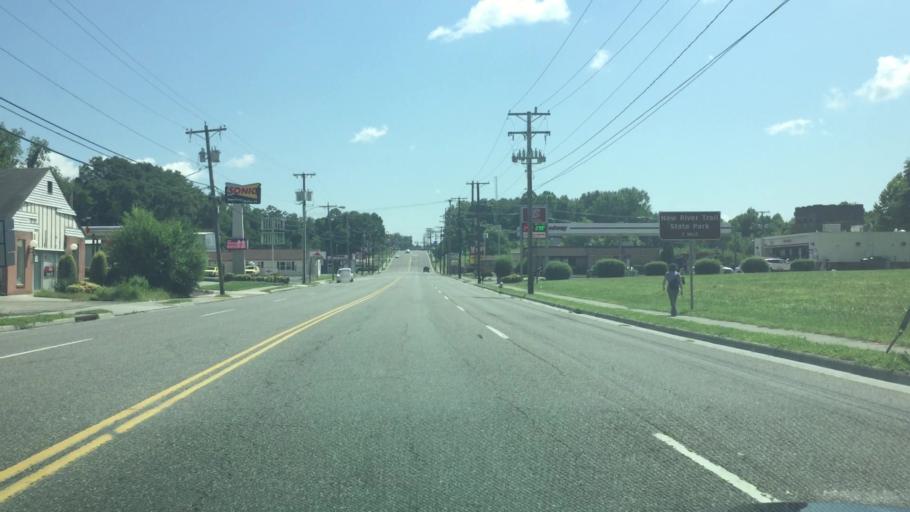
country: US
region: Virginia
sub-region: Pulaski County
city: Pulaski
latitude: 37.0486
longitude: -80.7695
